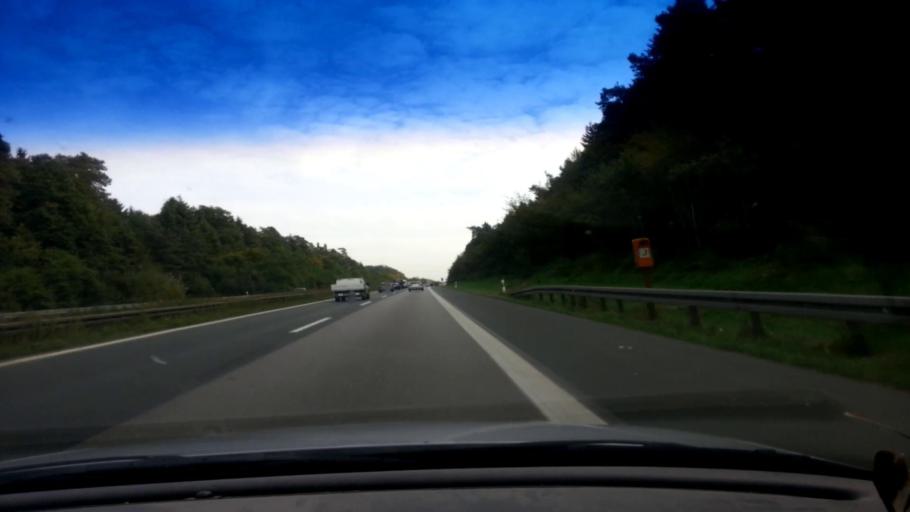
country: DE
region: Bavaria
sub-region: Upper Franconia
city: Strullendorf
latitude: 49.8528
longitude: 10.9844
